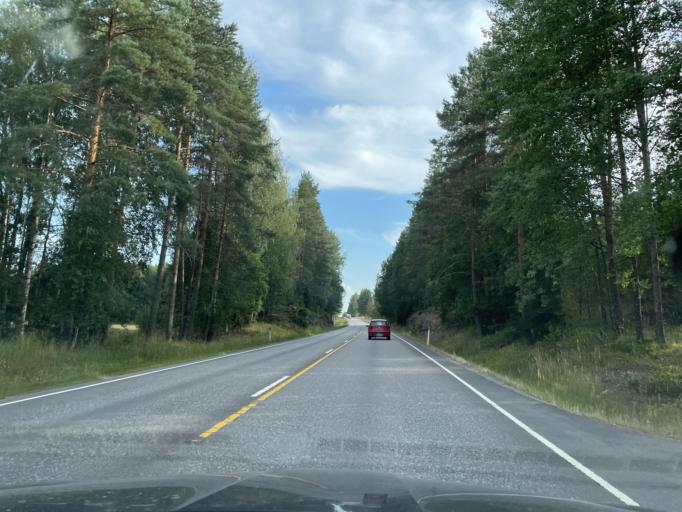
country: FI
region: Paijanne Tavastia
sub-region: Lahti
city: Padasjoki
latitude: 61.4215
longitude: 25.1823
